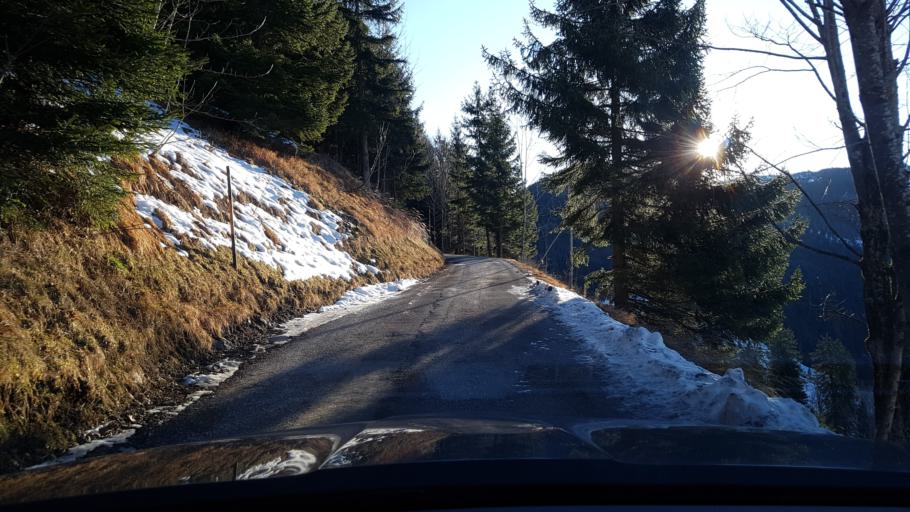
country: AT
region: Salzburg
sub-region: Politischer Bezirk Hallein
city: Scheffau am Tennengebirge
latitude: 47.6491
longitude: 13.2308
